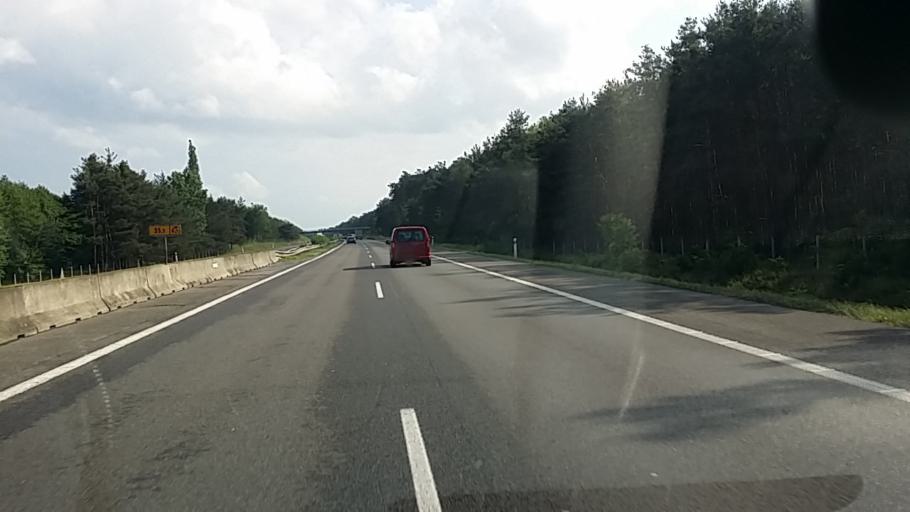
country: SK
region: Bratislavsky
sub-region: Okres Malacky
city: Malacky
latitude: 48.3751
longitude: 17.0203
